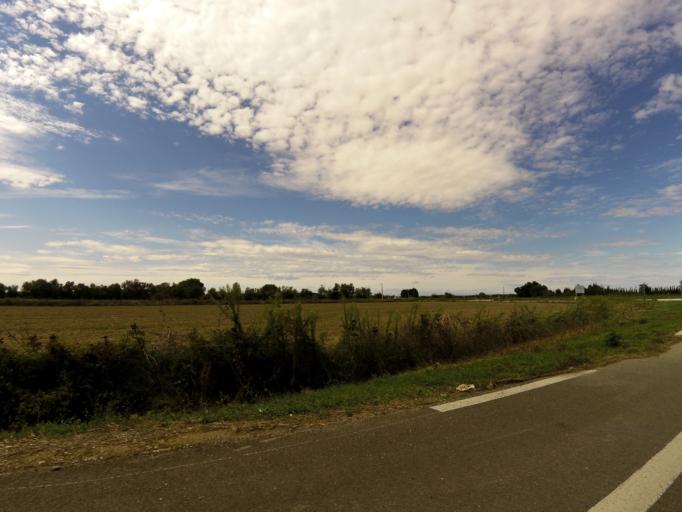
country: FR
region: Languedoc-Roussillon
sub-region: Departement du Gard
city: Aimargues
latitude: 43.6573
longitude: 4.2033
